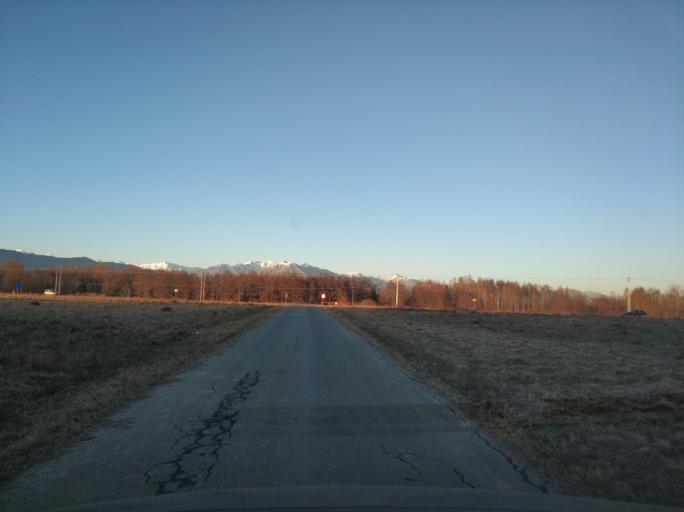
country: IT
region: Piedmont
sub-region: Provincia di Torino
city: San Francesco al Campo
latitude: 45.2484
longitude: 7.6430
